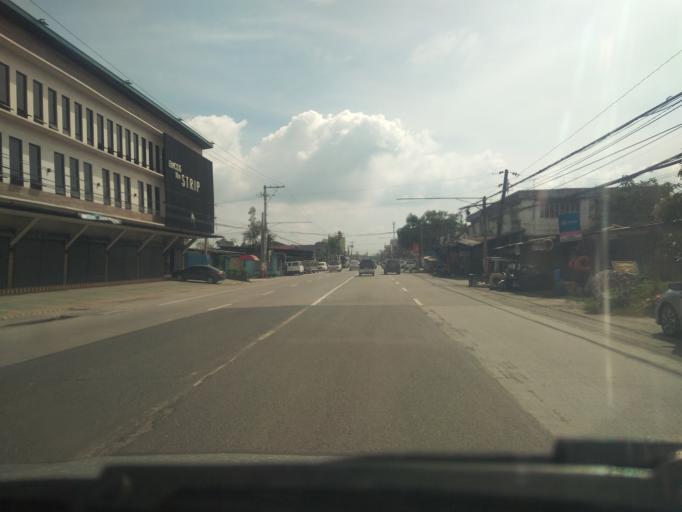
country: PH
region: Central Luzon
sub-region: Province of Pampanga
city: San Fernando
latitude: 15.0133
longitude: 120.7060
